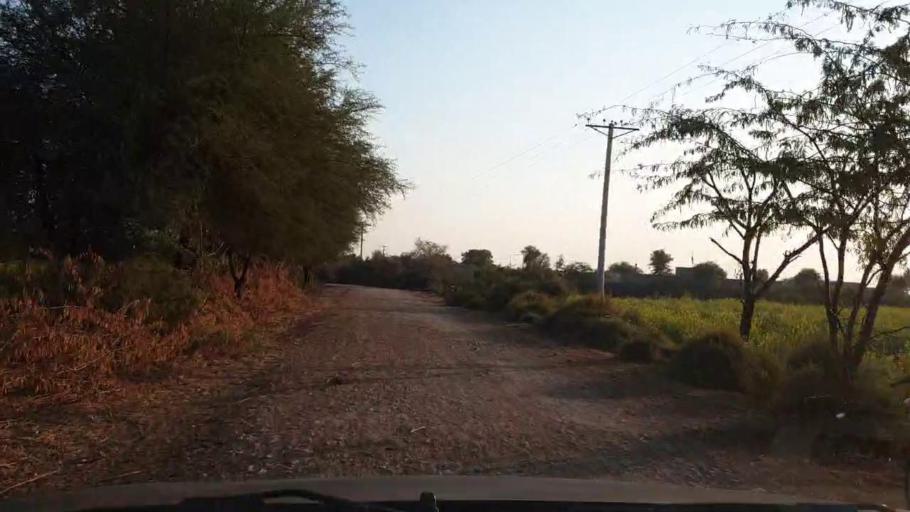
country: PK
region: Sindh
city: Jhol
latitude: 25.9199
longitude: 68.9336
